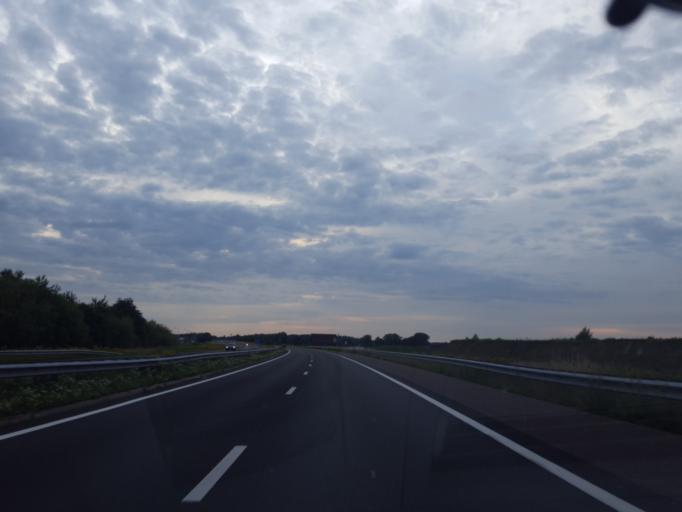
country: NL
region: Overijssel
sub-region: Gemeente Steenwijkerland
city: Steenwijk
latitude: 52.7955
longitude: 6.1444
